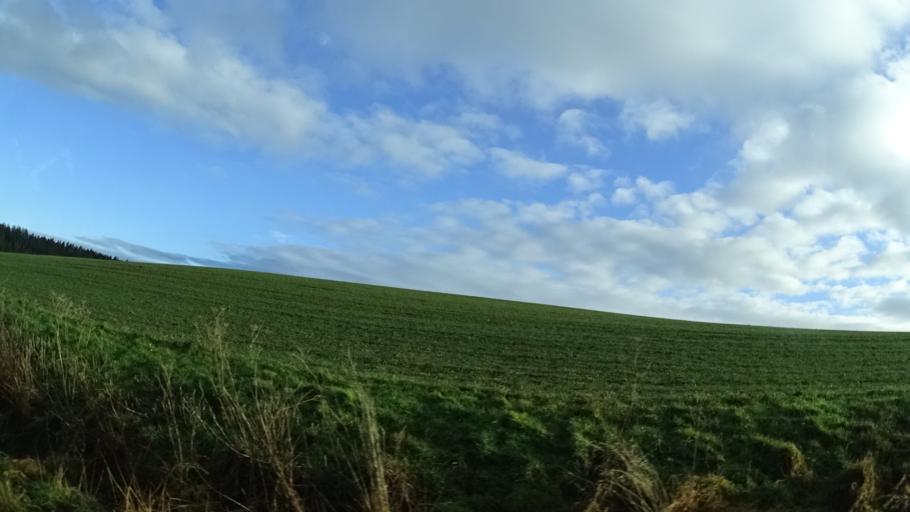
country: DE
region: Thuringia
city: Plaue
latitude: 50.8132
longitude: 10.8902
